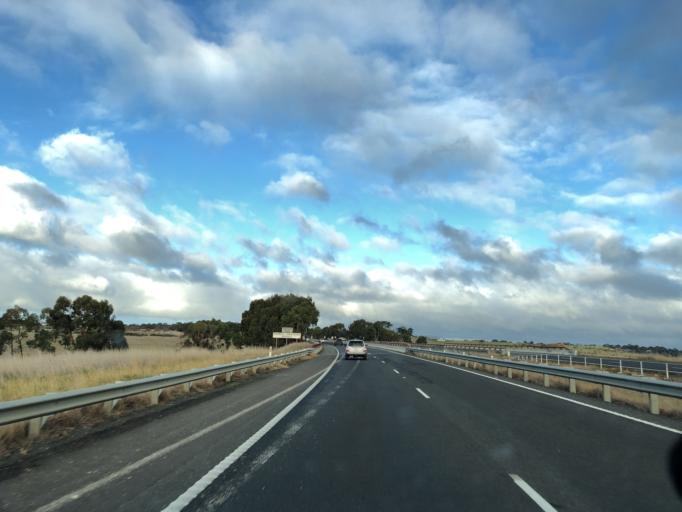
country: AU
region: Victoria
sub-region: Mount Alexander
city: Castlemaine
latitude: -37.2215
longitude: 144.4182
